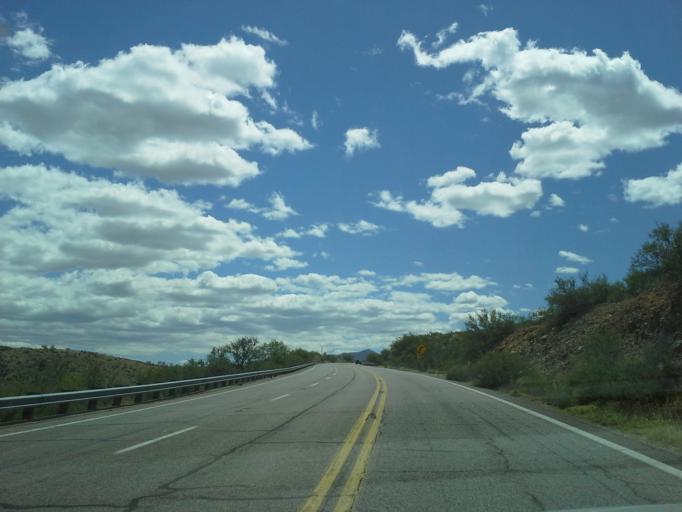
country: US
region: Arizona
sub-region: Pinal County
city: Oracle
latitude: 32.6429
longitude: -110.7233
